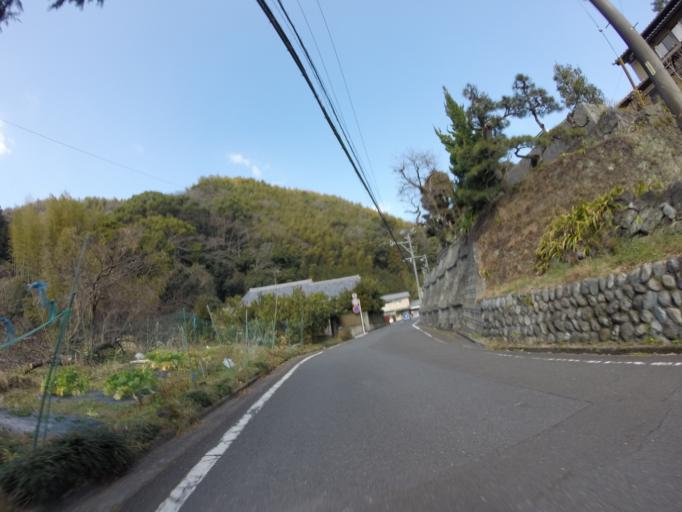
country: JP
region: Shizuoka
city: Shizuoka-shi
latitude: 35.0590
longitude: 138.4977
